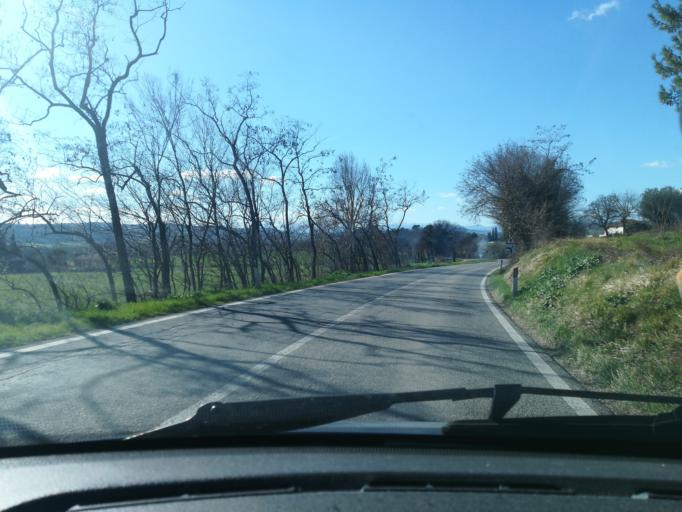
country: IT
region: The Marches
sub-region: Provincia di Macerata
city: Montecassiano
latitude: 43.3548
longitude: 13.4396
